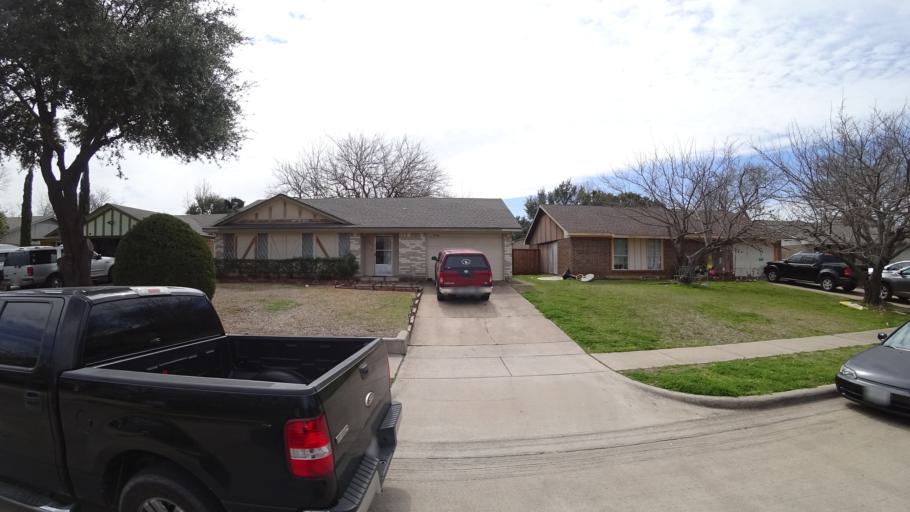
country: US
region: Texas
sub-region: Denton County
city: Lewisville
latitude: 33.0363
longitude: -97.0165
